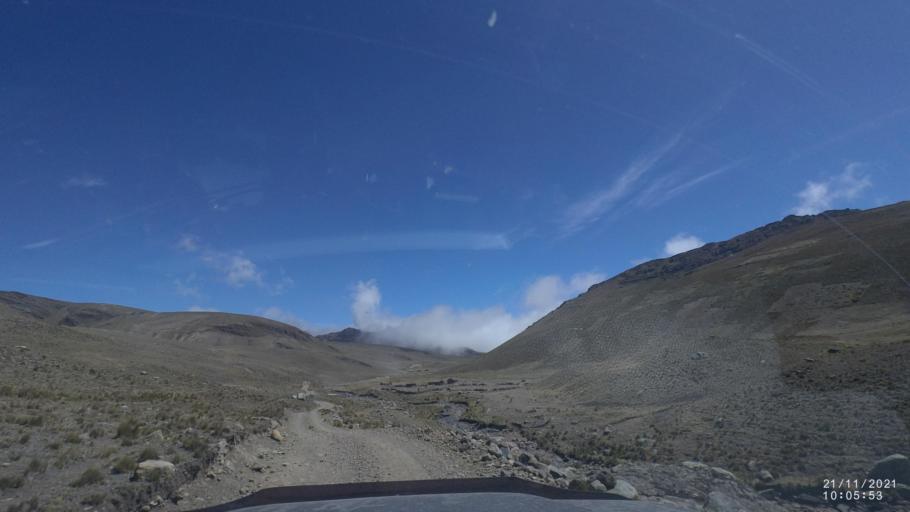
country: BO
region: Cochabamba
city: Cochabamba
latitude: -17.0166
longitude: -66.2854
